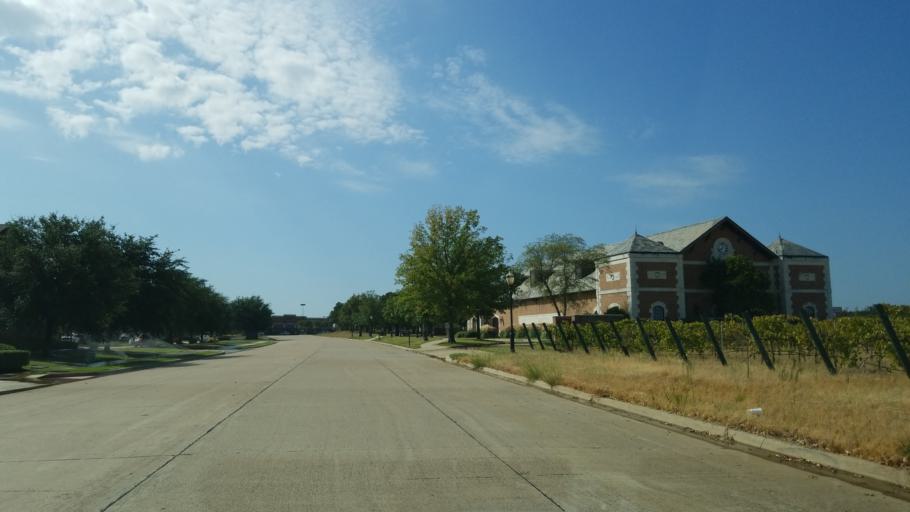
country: US
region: Texas
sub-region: Tarrant County
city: Grapevine
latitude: 32.8868
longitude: -97.0968
